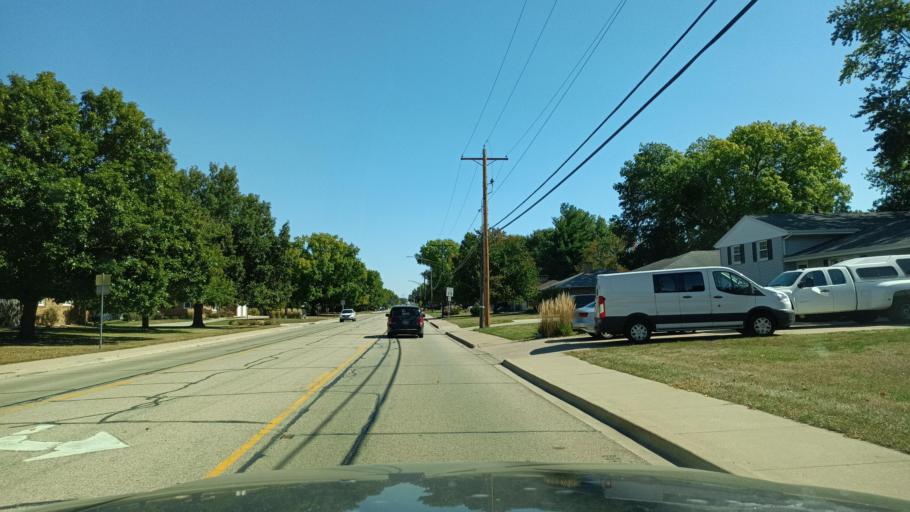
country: US
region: Illinois
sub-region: Tazewell County
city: Morton
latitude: 40.6130
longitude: -89.4495
